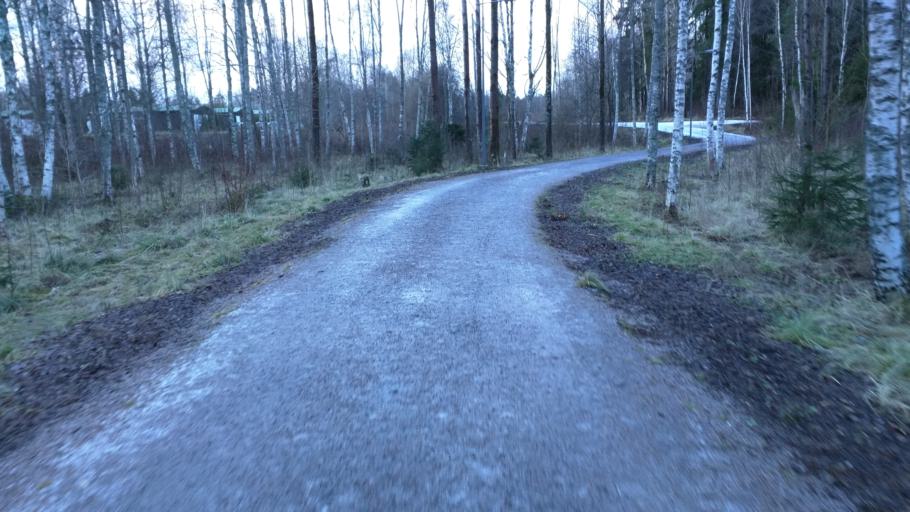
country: FI
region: Uusimaa
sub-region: Helsinki
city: Kauniainen
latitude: 60.2387
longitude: 24.7310
